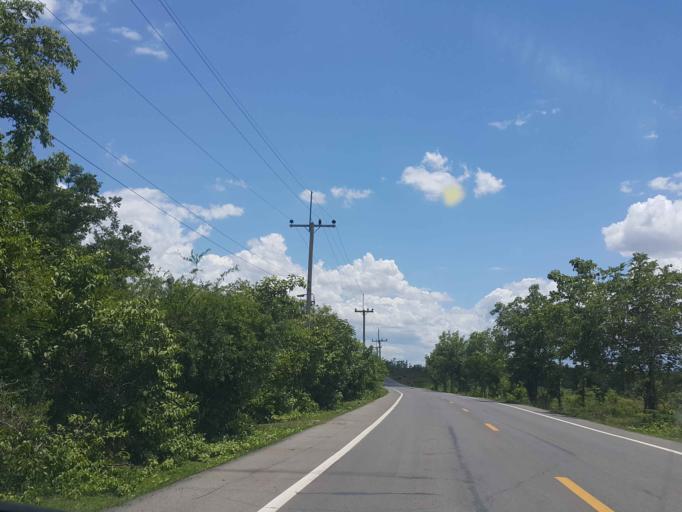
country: TH
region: Phrae
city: Nong Muang Khai
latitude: 18.1987
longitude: 100.2236
